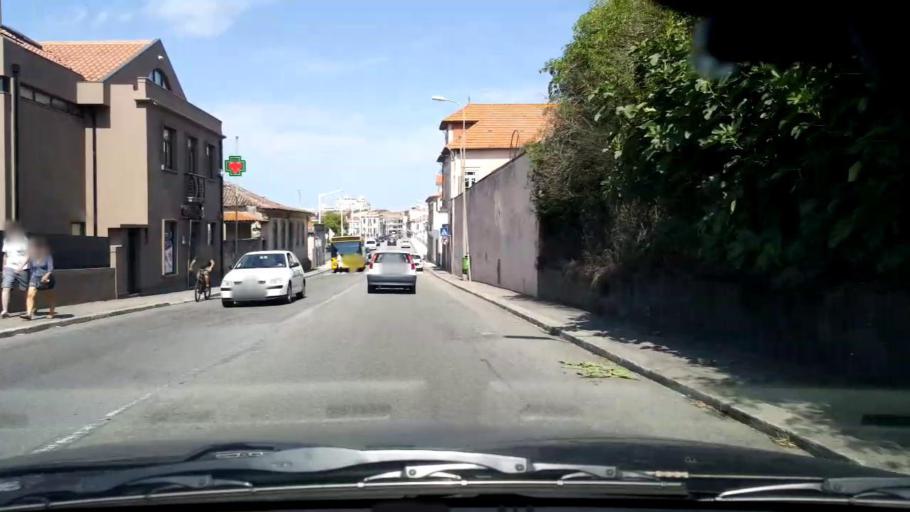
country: PT
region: Porto
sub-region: Vila do Conde
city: Vila do Conde
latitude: 41.3498
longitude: -8.7387
